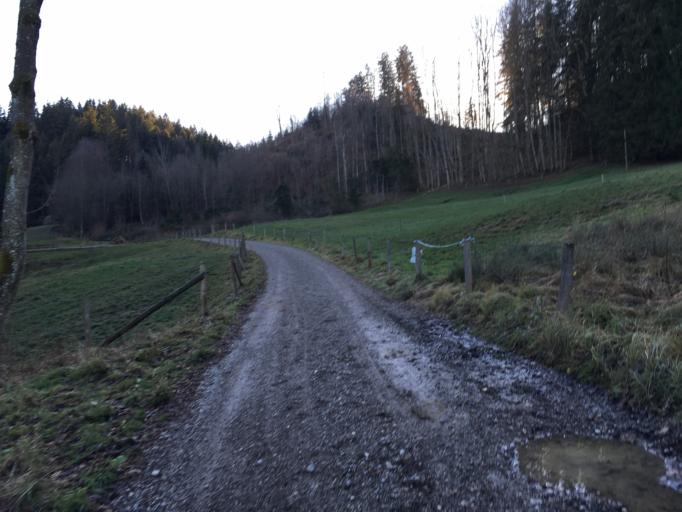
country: DE
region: Bavaria
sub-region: Swabia
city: Bohen
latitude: 47.8673
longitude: 10.2907
